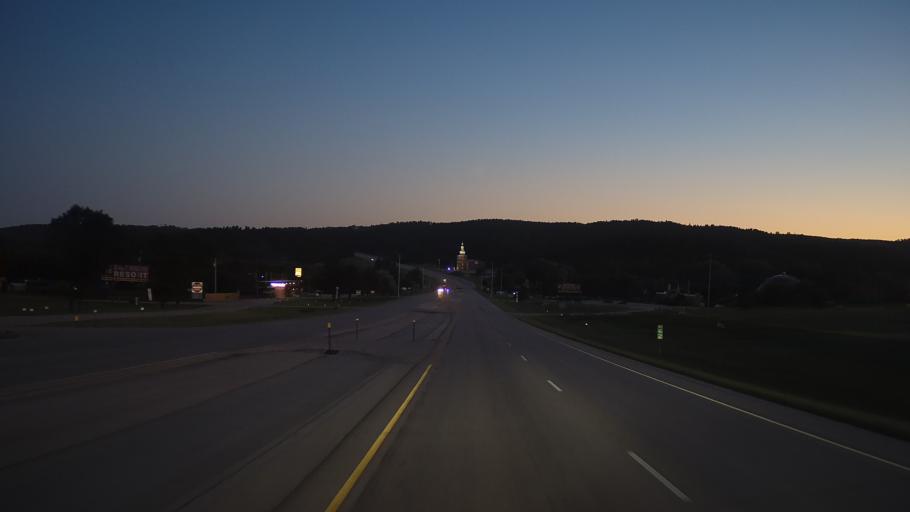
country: US
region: South Dakota
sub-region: Pennington County
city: Colonial Pine Hills
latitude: 43.9934
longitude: -103.2684
